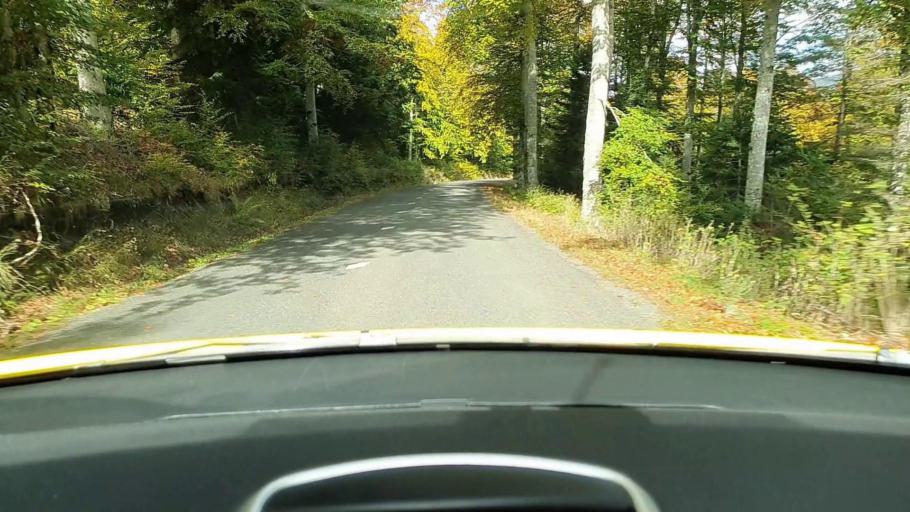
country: FR
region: Languedoc-Roussillon
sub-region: Departement du Gard
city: Valleraugue
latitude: 44.0723
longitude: 3.5678
